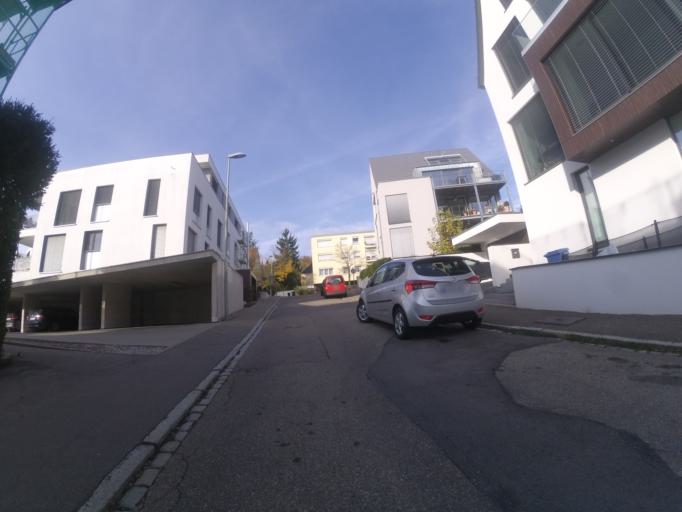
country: DE
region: Baden-Wuerttemberg
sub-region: Tuebingen Region
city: Ulm
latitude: 48.4071
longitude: 9.9824
